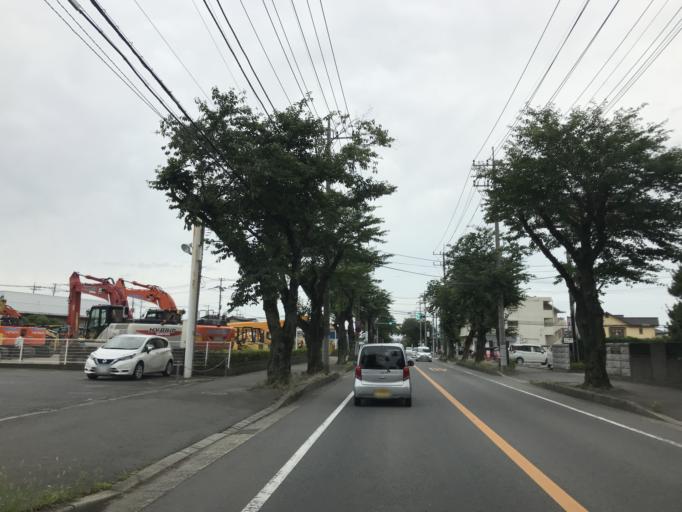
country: JP
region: Ibaraki
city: Mito-shi
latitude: 36.3291
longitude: 140.4588
